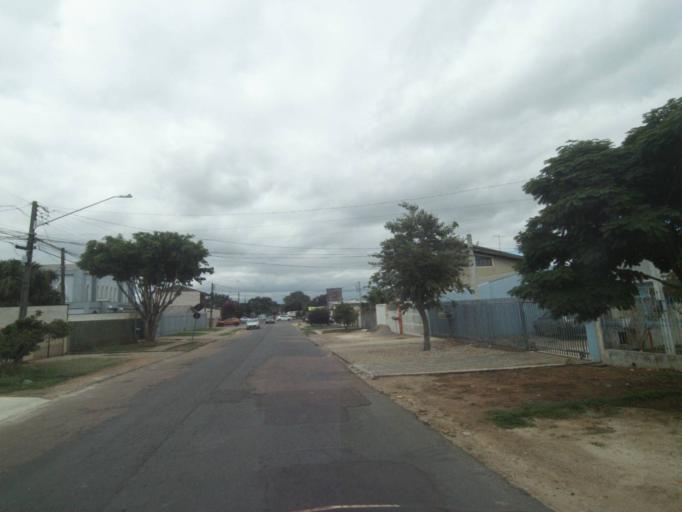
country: BR
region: Parana
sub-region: Sao Jose Dos Pinhais
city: Sao Jose dos Pinhais
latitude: -25.5528
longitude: -49.2533
